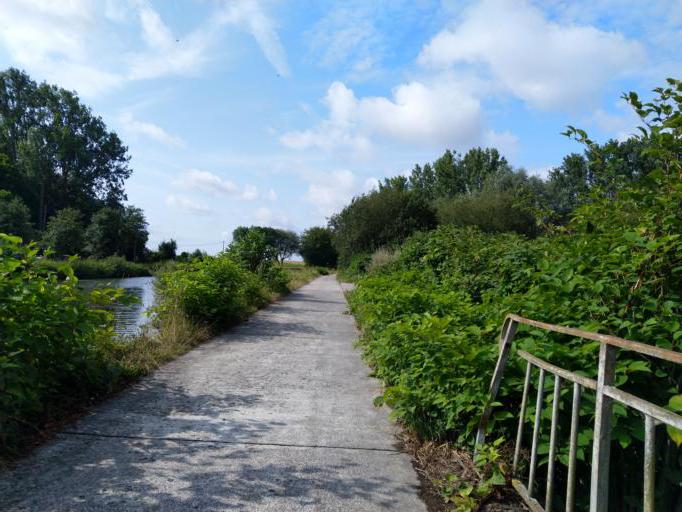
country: BE
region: Wallonia
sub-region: Province du Hainaut
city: Chievres
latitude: 50.5842
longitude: 3.7801
